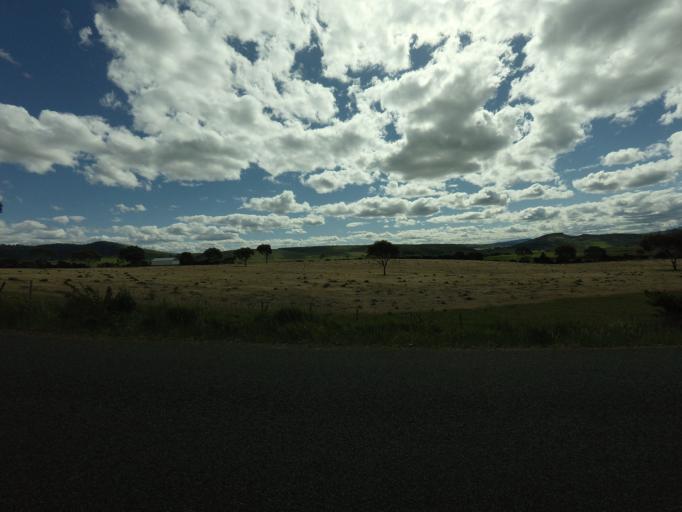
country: AU
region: Tasmania
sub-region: Brighton
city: Bridgewater
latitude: -42.3910
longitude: 147.3149
